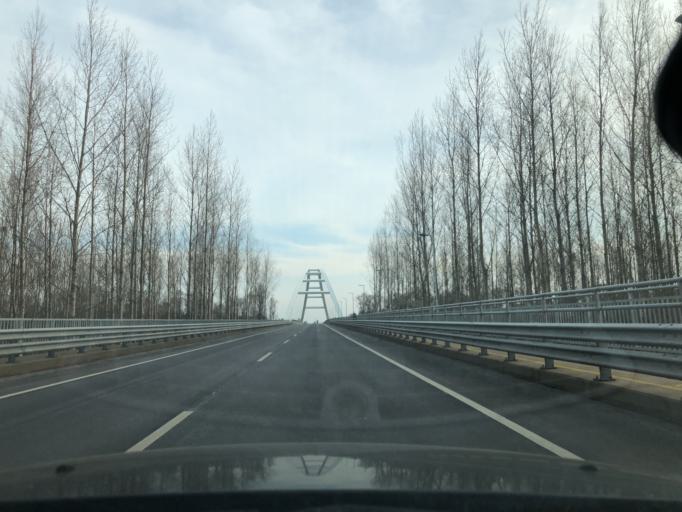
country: HU
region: Gyor-Moson-Sopron
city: Gyor
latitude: 47.7293
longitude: 17.6996
